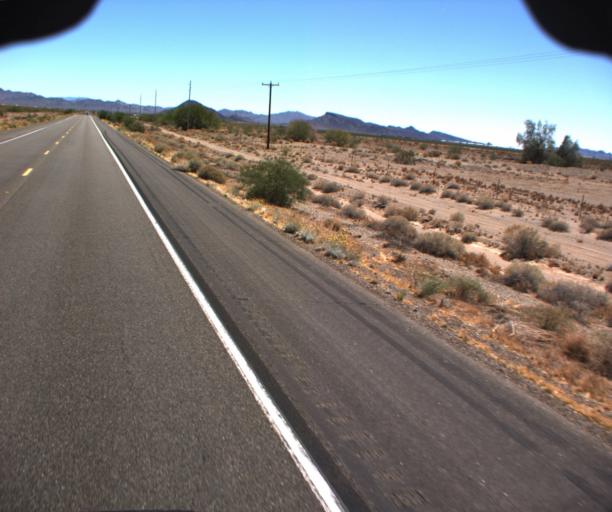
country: US
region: Arizona
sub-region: La Paz County
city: Salome
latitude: 33.7104
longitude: -113.8093
